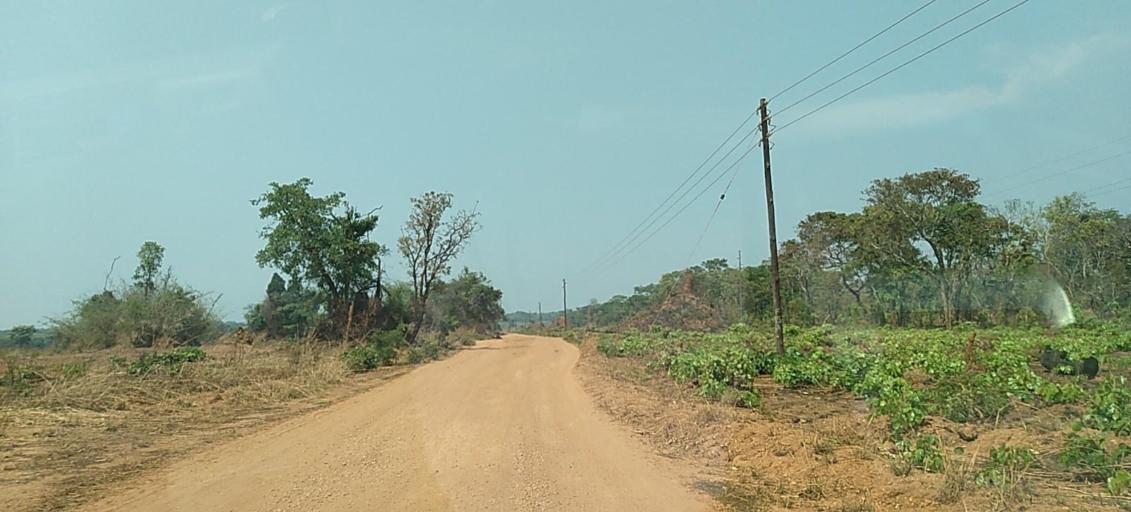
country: ZM
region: Copperbelt
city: Chingola
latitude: -13.0587
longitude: 27.4227
